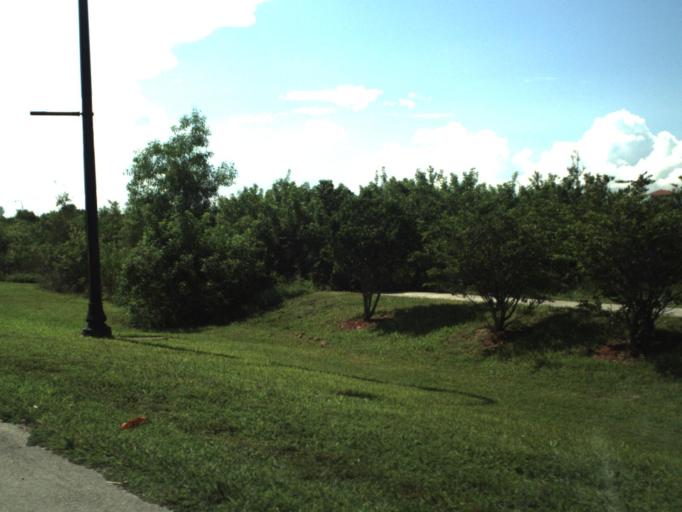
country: US
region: Florida
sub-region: Miami-Dade County
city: Country Club
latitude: 25.9837
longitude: -80.2984
